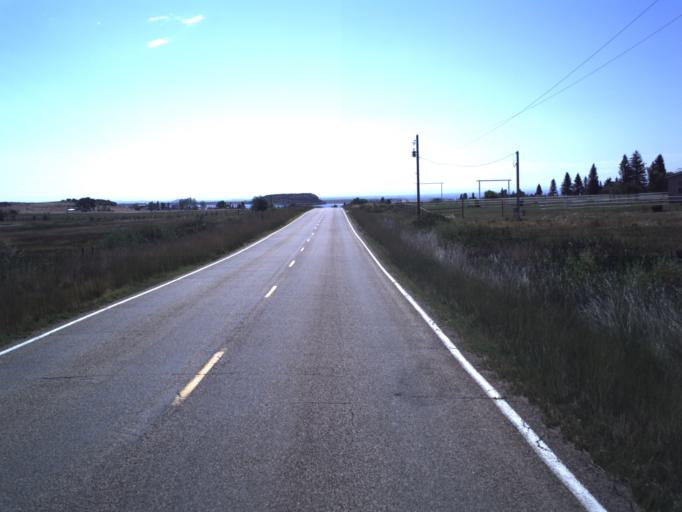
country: US
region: Utah
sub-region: Duchesne County
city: Duchesne
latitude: 40.3117
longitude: -110.2484
